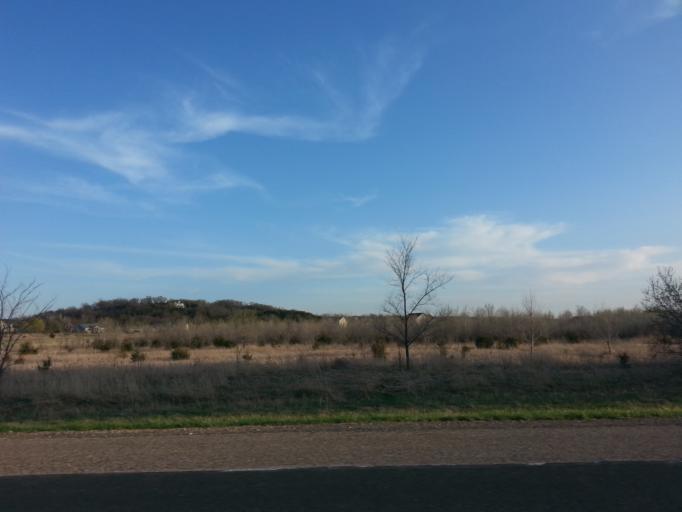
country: US
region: Minnesota
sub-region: Washington County
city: Lake Saint Croix Beach
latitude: 44.9310
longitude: -92.7045
